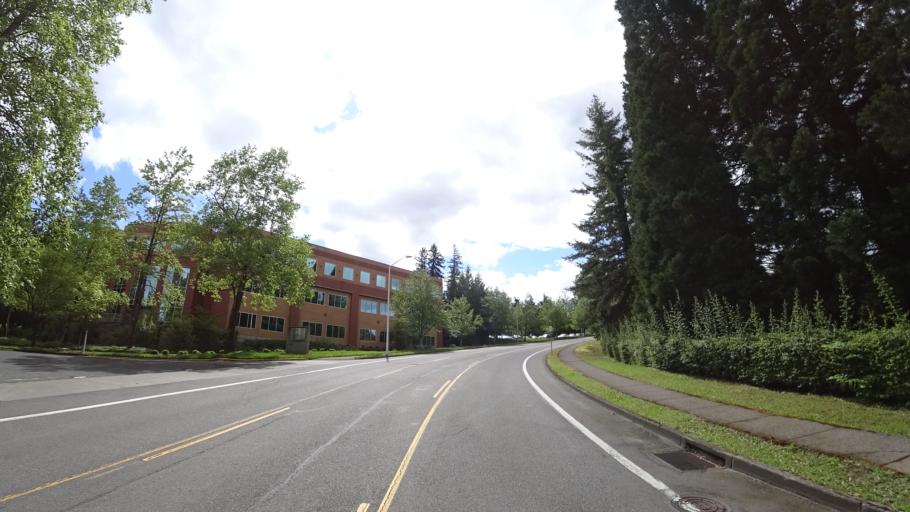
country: US
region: Oregon
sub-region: Washington County
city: Metzger
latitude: 45.4384
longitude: -122.7465
